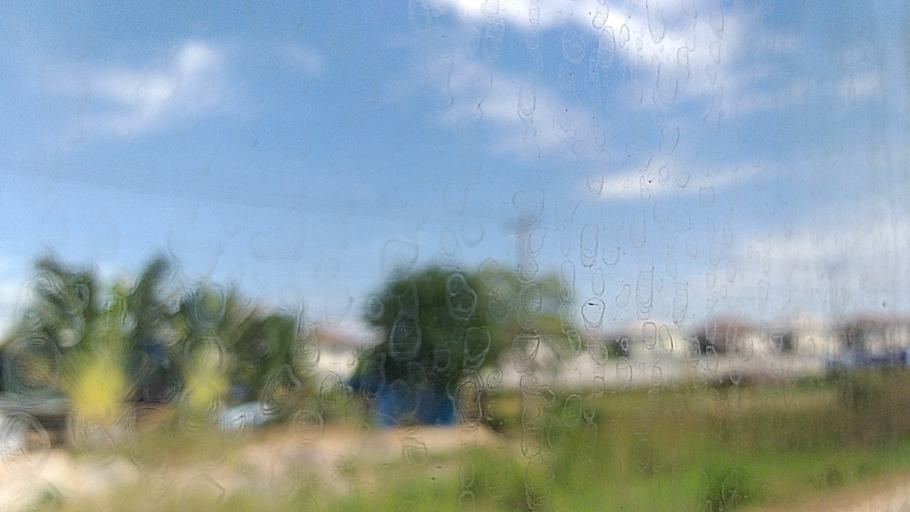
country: TH
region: Khon Kaen
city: Khon Kaen
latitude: 16.4026
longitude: 102.8760
